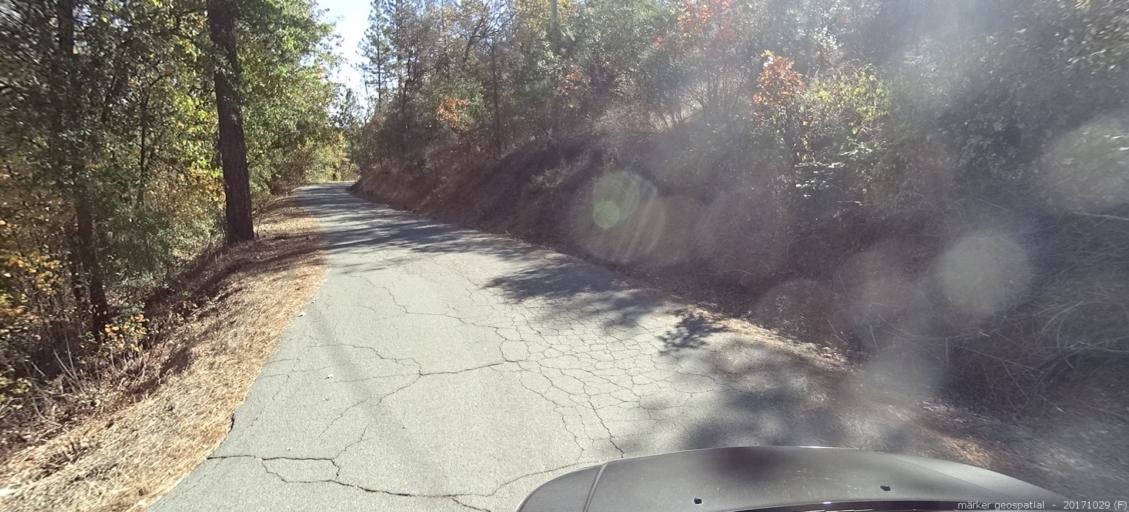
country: US
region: California
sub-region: Shasta County
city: Shasta
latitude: 40.4900
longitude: -122.6848
